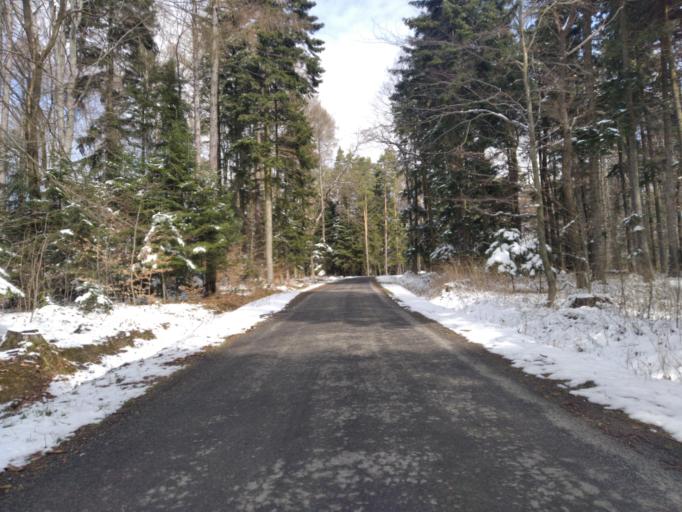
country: PL
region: Subcarpathian Voivodeship
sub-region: Powiat ropczycko-sedziszowski
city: Ropczyce
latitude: 50.0127
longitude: 21.5969
